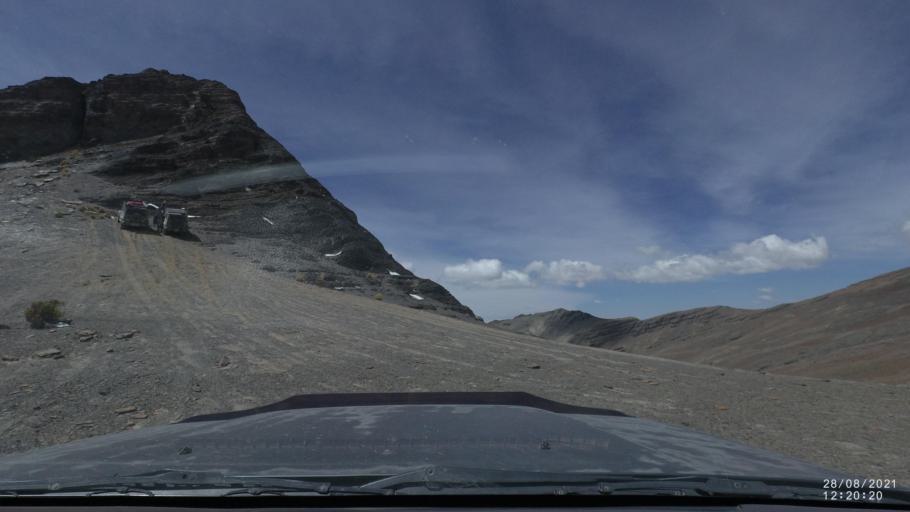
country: BO
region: Cochabamba
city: Sipe Sipe
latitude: -17.2819
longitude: -66.3818
